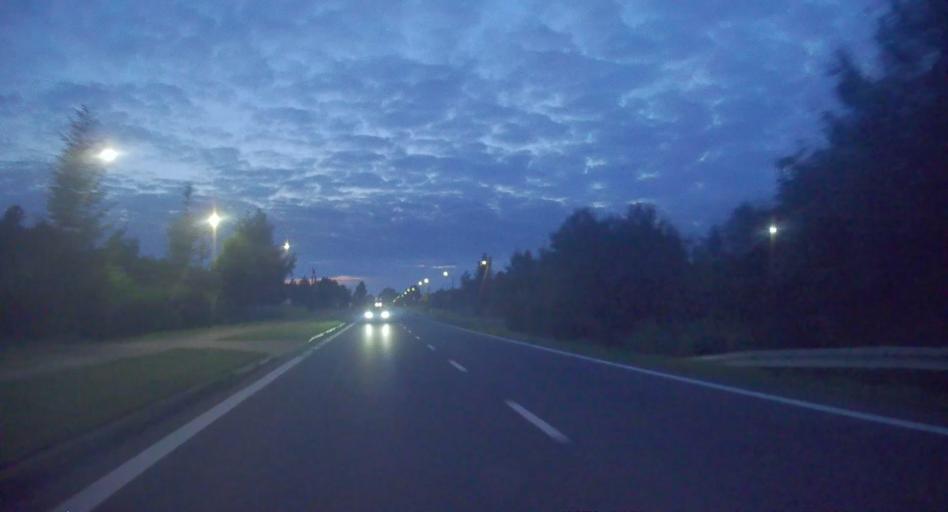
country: PL
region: Silesian Voivodeship
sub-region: Powiat klobucki
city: Kamyk
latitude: 50.8664
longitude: 19.0155
